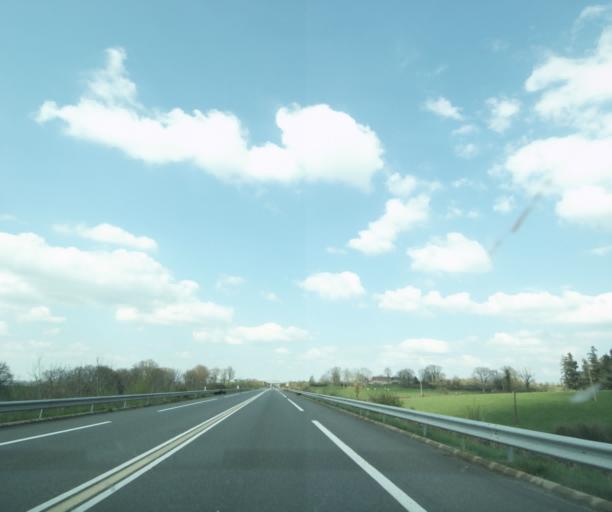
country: FR
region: Auvergne
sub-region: Departement de l'Allier
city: Montmarault
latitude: 46.3865
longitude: 3.0323
